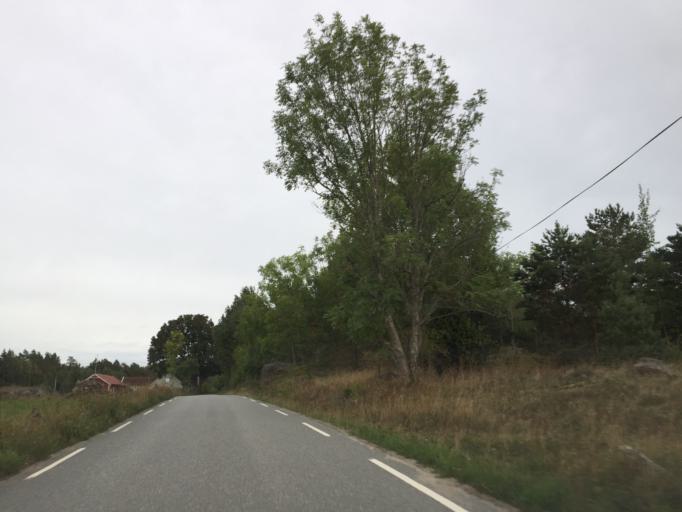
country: NO
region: Ostfold
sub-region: Hvaler
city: Skjaerhalden
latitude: 59.0714
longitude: 11.0047
